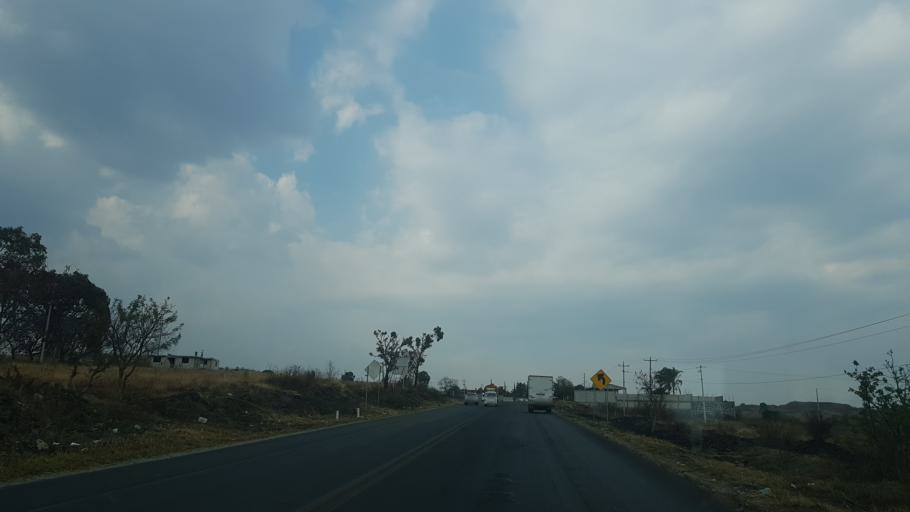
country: MX
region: Puebla
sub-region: Santa Isabel Cholula
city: Santa Ana Acozautla
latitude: 18.9663
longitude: -98.3840
